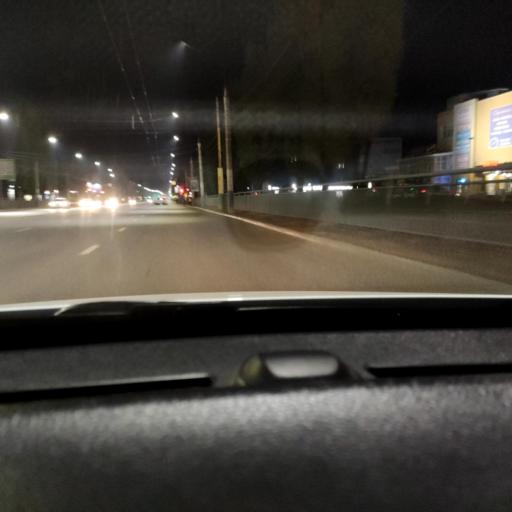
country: RU
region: Voronezj
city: Voronezh
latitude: 51.6884
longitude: 39.2660
